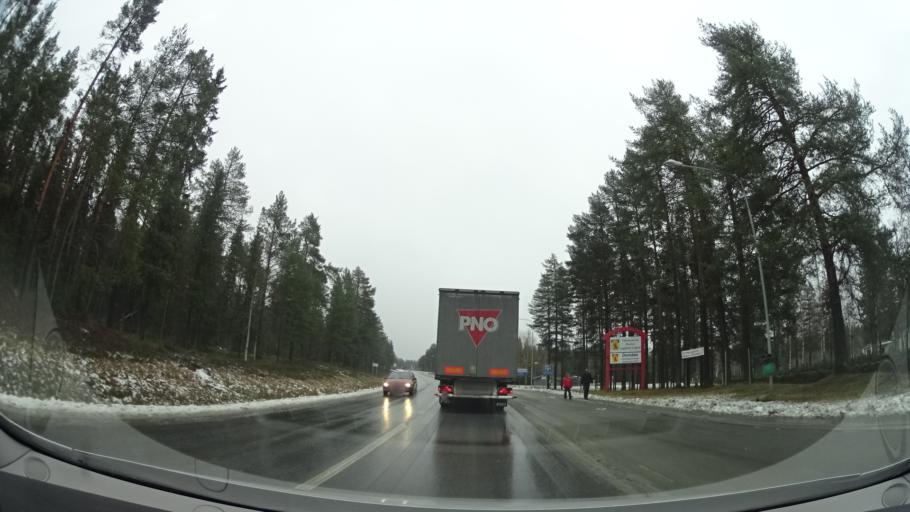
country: SE
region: Vaesterbotten
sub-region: Dorotea Kommun
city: Dorotea
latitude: 64.2593
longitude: 16.3782
